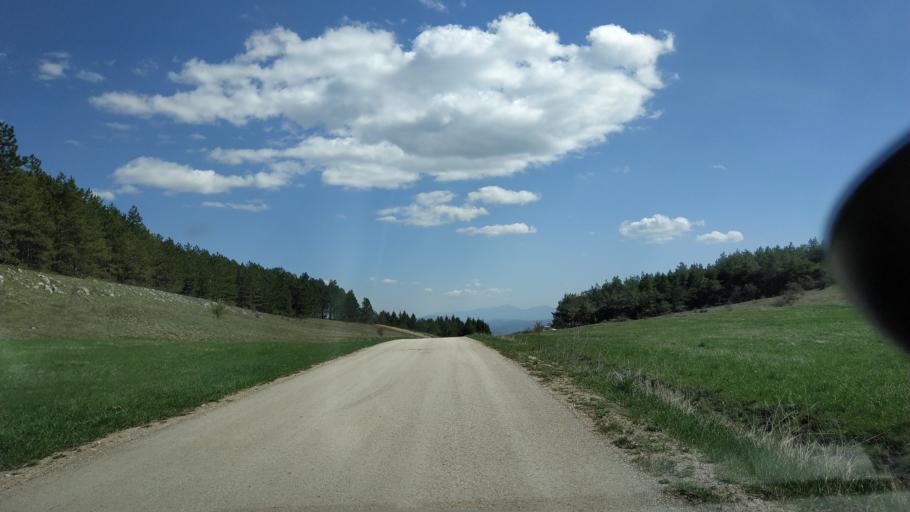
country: RS
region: Central Serbia
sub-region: Zajecarski Okrug
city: Soko Banja
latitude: 43.5919
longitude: 21.8870
